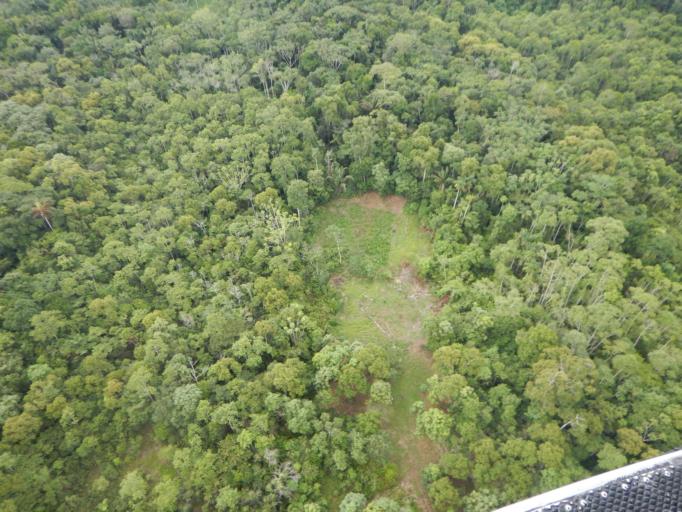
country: BO
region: Cochabamba
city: Chimore
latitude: -16.9998
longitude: -65.0605
